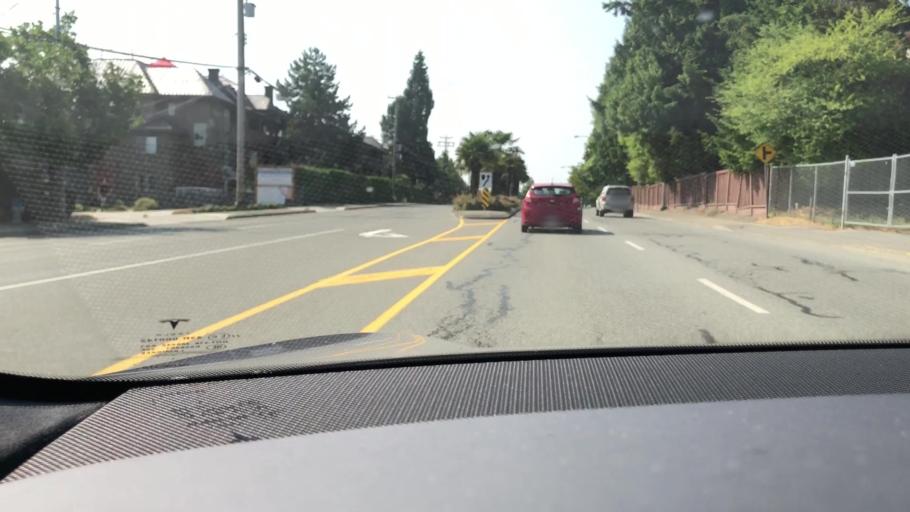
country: US
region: Washington
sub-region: Whatcom County
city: Point Roberts
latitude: 49.0295
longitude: -123.0687
